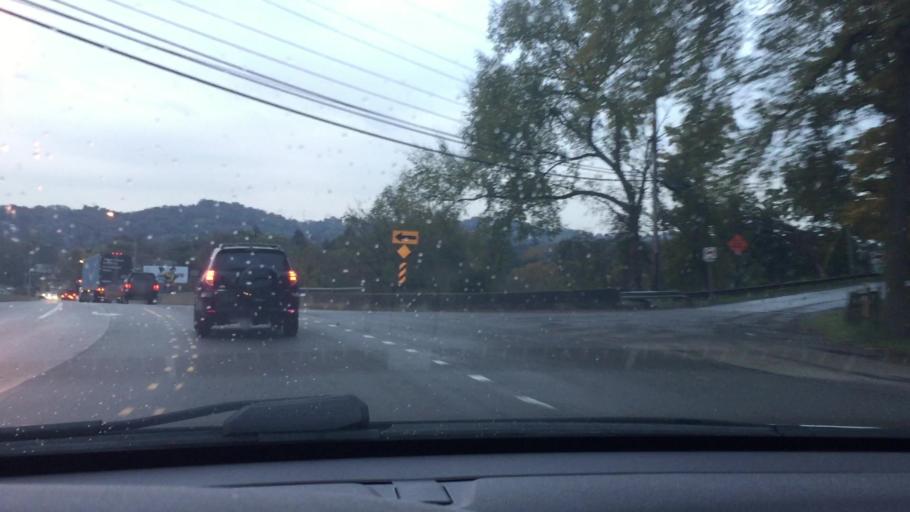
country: US
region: Pennsylvania
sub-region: Allegheny County
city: Ingram
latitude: 40.4400
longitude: -80.0840
